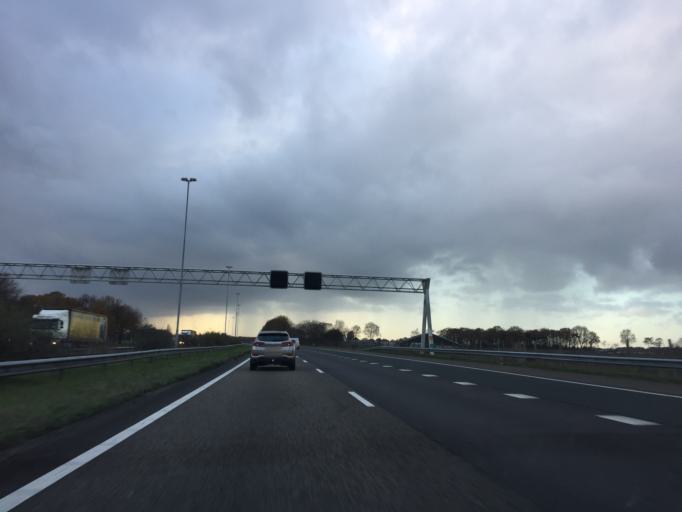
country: NL
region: North Brabant
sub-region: Gemeente Dongen
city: Dongen
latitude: 51.5592
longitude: 4.8819
